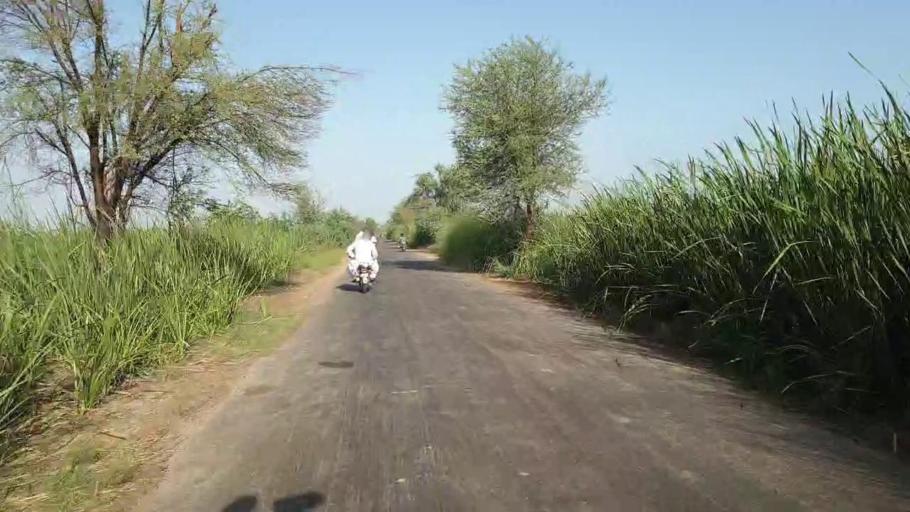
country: PK
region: Sindh
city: Nawabshah
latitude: 26.3752
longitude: 68.4651
